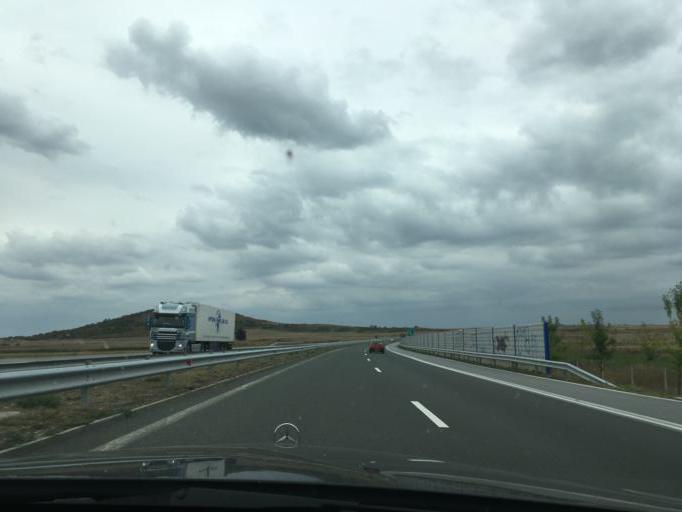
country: BG
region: Yambol
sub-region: Obshtina Yambol
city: Yambol
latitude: 42.5451
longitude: 26.4509
